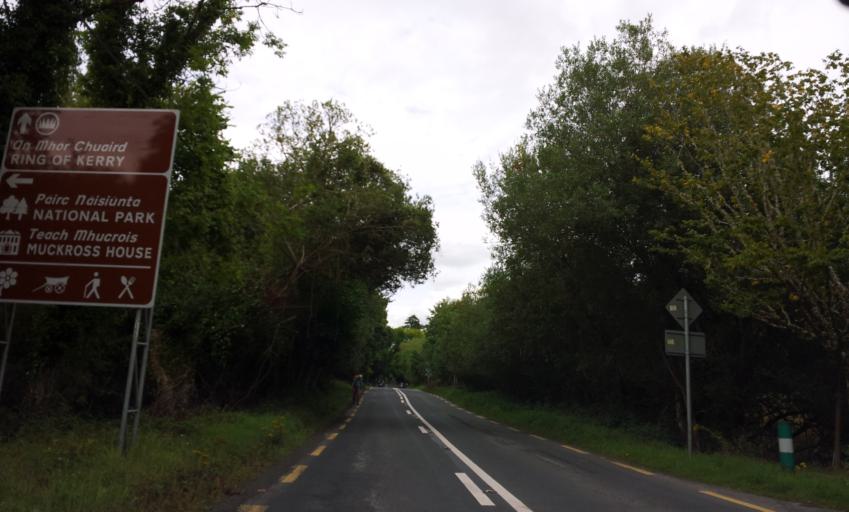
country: IE
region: Munster
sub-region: Ciarrai
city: Cill Airne
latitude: 52.0155
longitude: -9.4944
